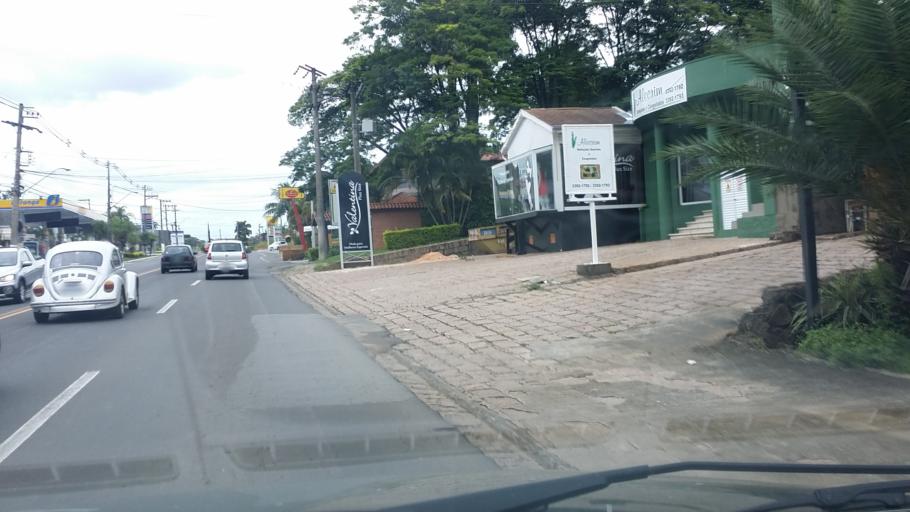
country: BR
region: Sao Paulo
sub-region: Indaiatuba
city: Indaiatuba
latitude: -23.0998
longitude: -47.1849
